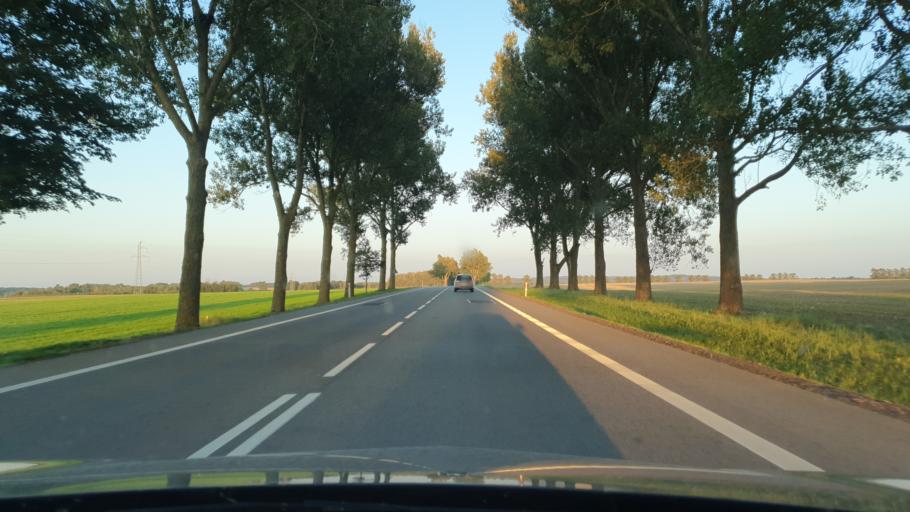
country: PL
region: Pomeranian Voivodeship
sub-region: Powiat slupski
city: Potegowo
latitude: 54.4778
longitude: 17.5246
